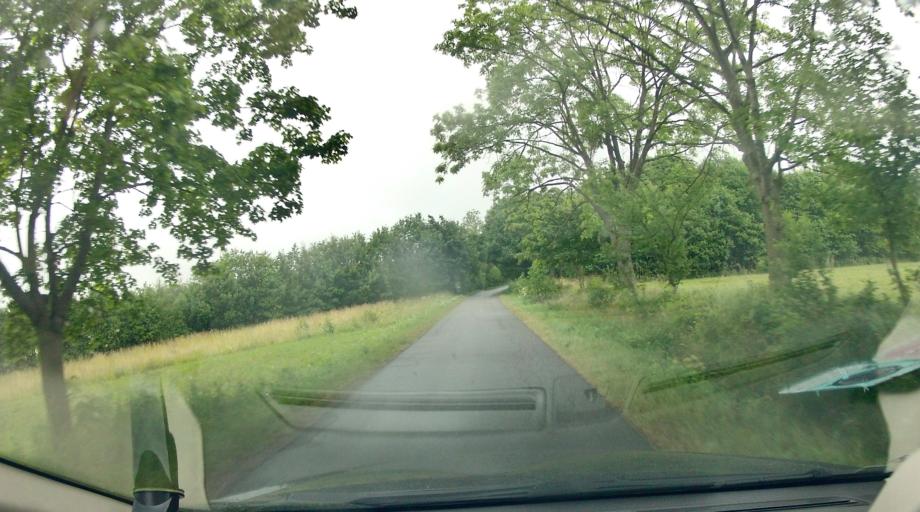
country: PL
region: Lower Silesian Voivodeship
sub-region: Powiat klodzki
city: Miedzylesie
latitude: 50.1807
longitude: 16.7217
